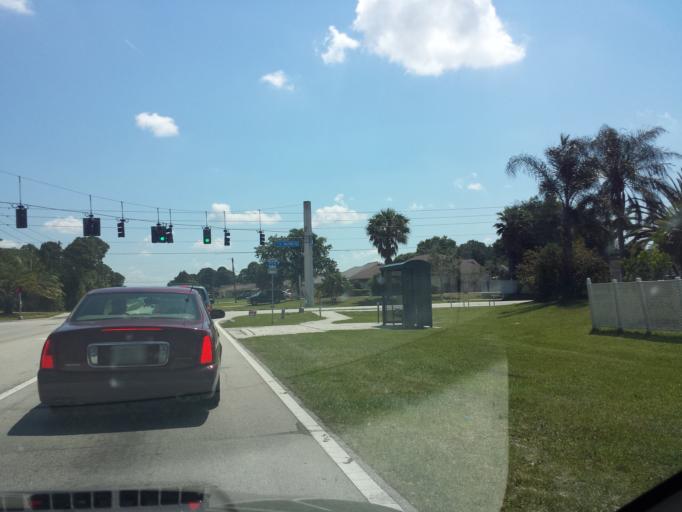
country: US
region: Florida
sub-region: Sarasota County
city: North Port
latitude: 27.0690
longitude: -82.1980
